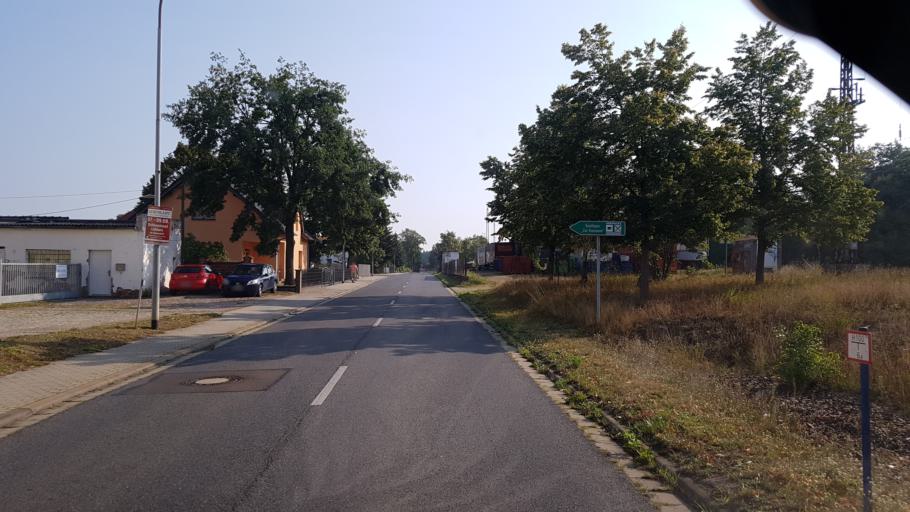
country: DE
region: Brandenburg
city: Drebkau
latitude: 51.6525
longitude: 14.2192
